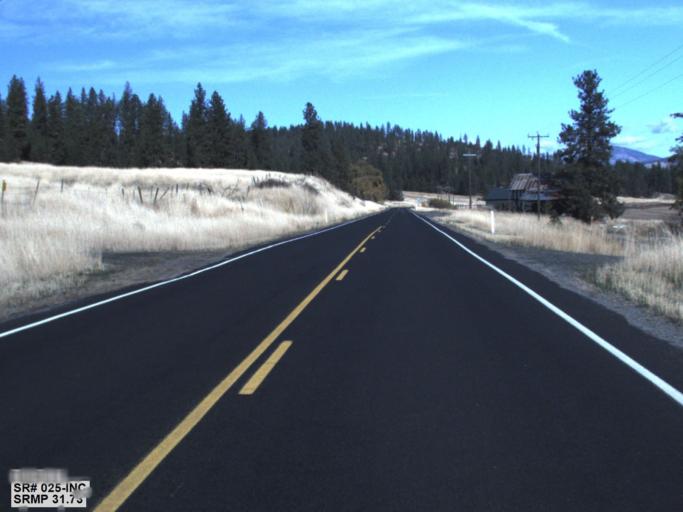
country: US
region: Washington
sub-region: Lincoln County
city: Davenport
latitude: 48.0030
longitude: -118.2743
